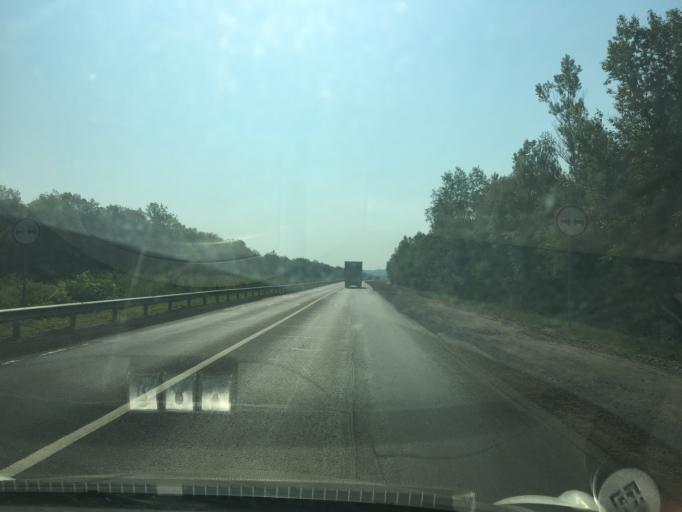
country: RU
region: Nizjnij Novgorod
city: Kstovo
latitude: 56.0927
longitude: 44.3250
